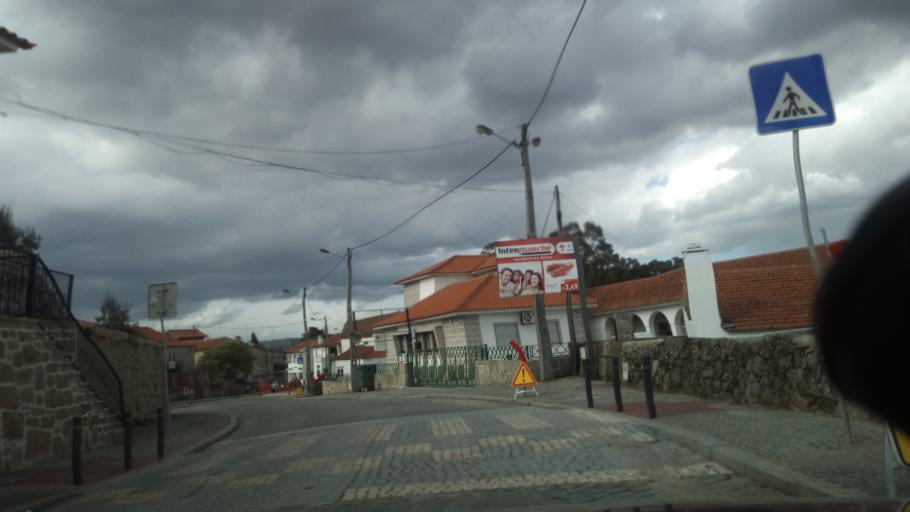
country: PT
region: Guarda
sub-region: Celorico da Beira
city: Celorico da Beira
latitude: 40.6395
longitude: -7.3881
